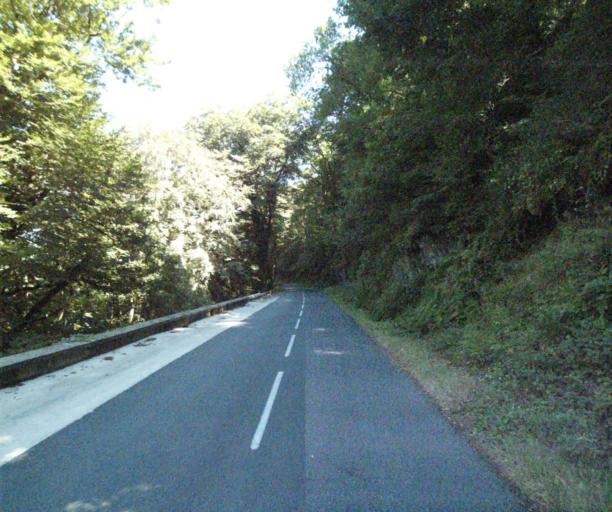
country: FR
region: Midi-Pyrenees
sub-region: Departement du Tarn
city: Soreze
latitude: 43.4376
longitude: 2.0877
